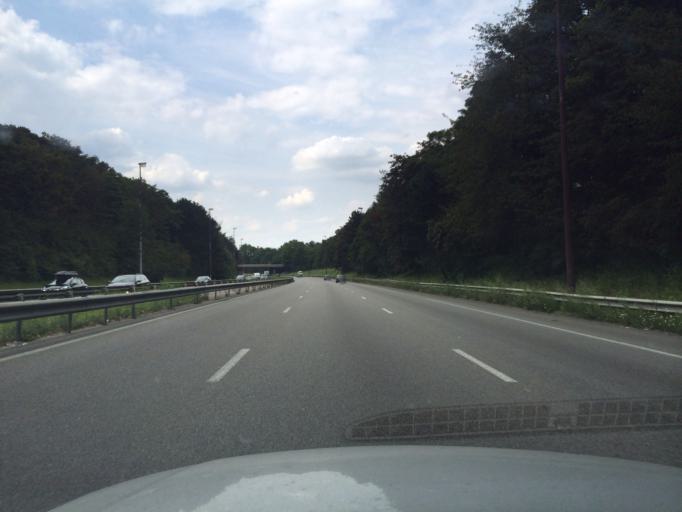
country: FR
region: Ile-de-France
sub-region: Departement des Hauts-de-Seine
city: Chatenay-Malabry
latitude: 48.7688
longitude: 2.2441
